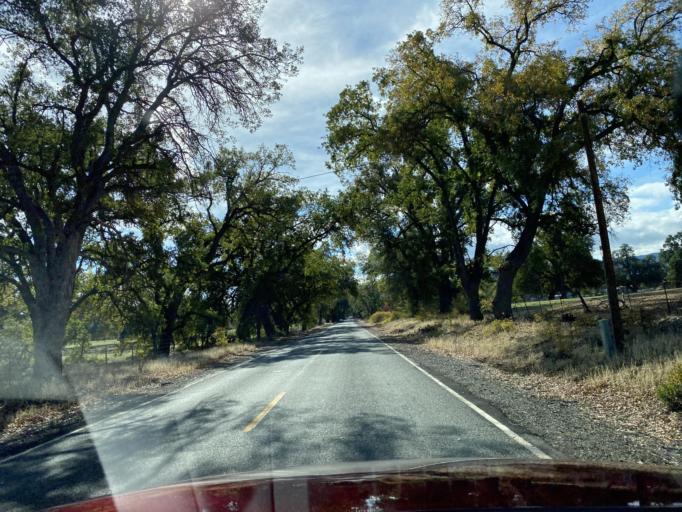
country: US
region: California
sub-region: Colusa County
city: Maxwell
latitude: 39.3966
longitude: -122.5519
